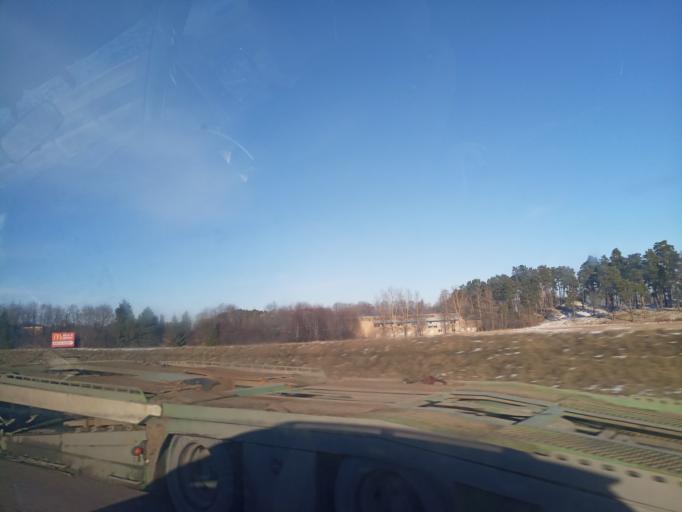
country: SE
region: Stockholm
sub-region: Upplands Vasby Kommun
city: Upplands Vaesby
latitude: 59.5360
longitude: 17.9125
